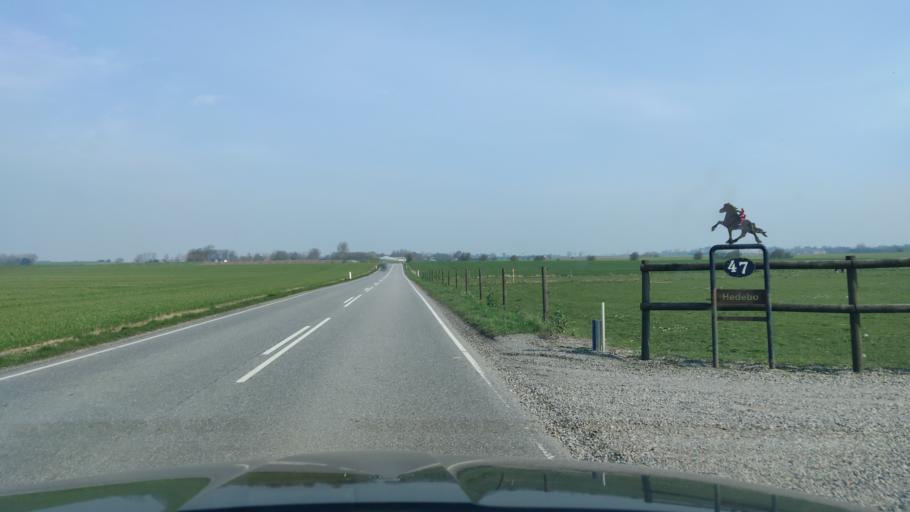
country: DK
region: South Denmark
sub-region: Nordfyns Kommune
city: Sonderso
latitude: 55.5005
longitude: 10.2493
